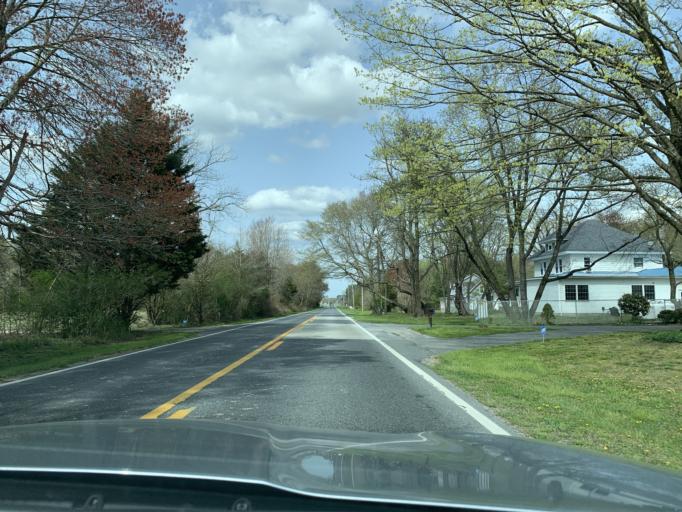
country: US
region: Delaware
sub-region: Sussex County
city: Georgetown
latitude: 38.6557
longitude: -75.3815
